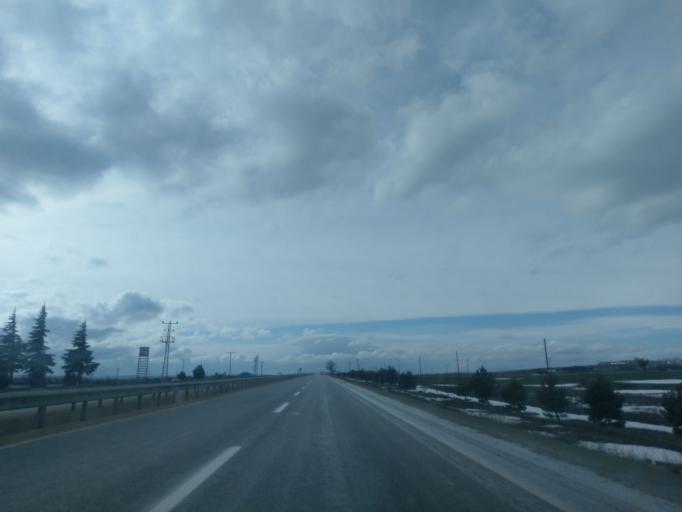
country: TR
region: Eskisehir
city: Inonu
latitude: 39.7214
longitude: 30.2367
